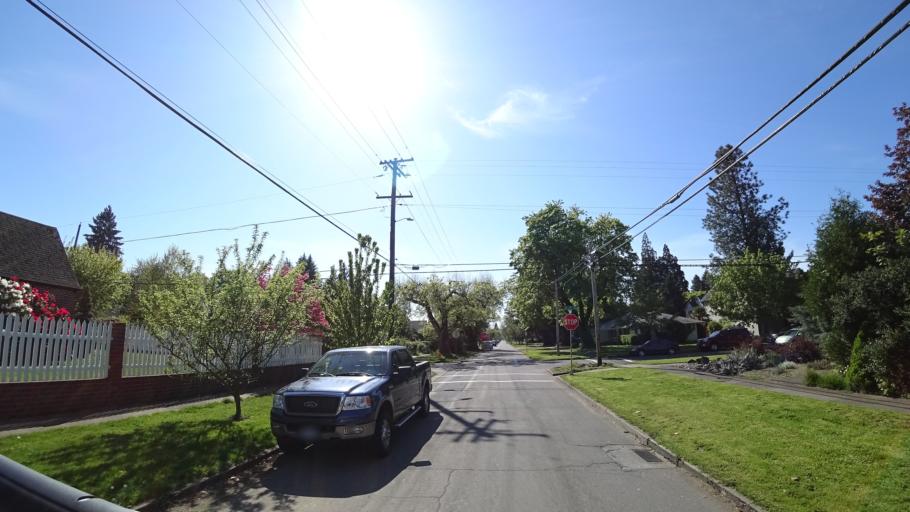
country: US
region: Oregon
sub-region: Washington County
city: Hillsboro
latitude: 45.5252
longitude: -122.9858
